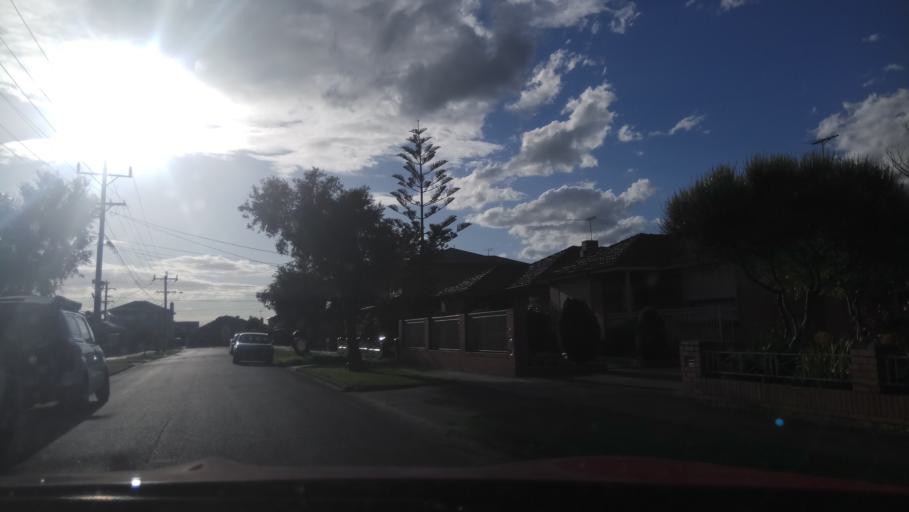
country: AU
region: Victoria
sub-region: Hobsons Bay
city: Altona North
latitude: -37.8285
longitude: 144.8450
